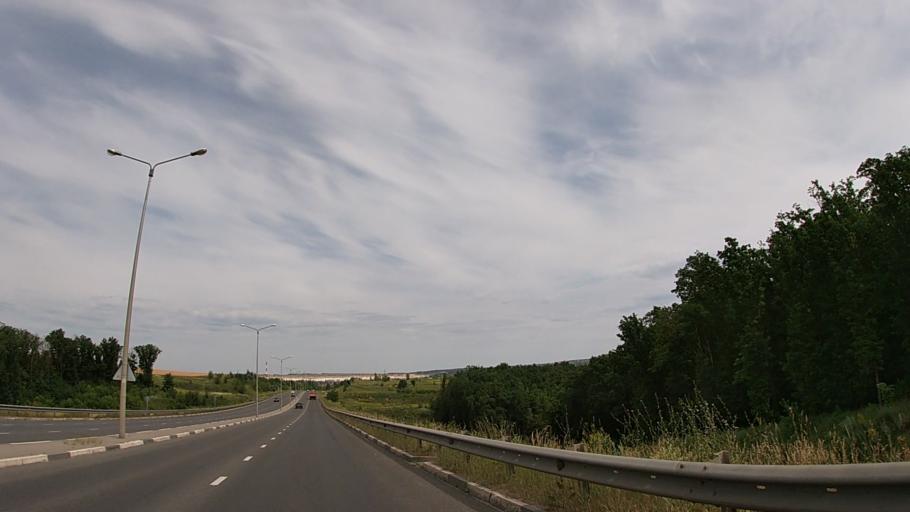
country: RU
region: Belgorod
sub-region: Belgorodskiy Rayon
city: Belgorod
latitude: 50.5992
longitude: 36.5303
